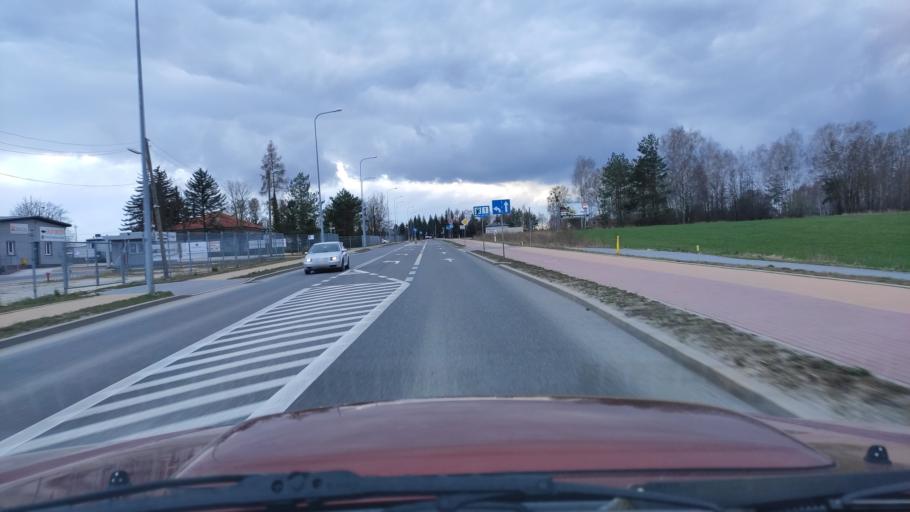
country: PL
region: Masovian Voivodeship
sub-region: Powiat zwolenski
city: Zwolen
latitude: 51.3746
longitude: 21.5911
